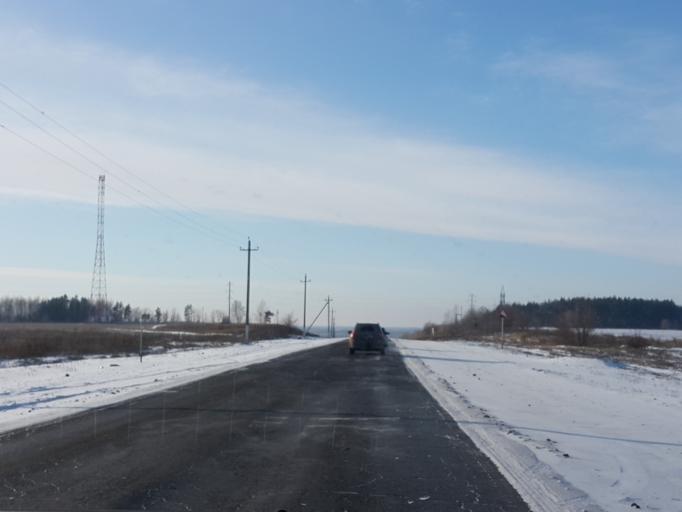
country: RU
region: Tambov
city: Znamenka
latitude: 52.4205
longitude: 41.4949
